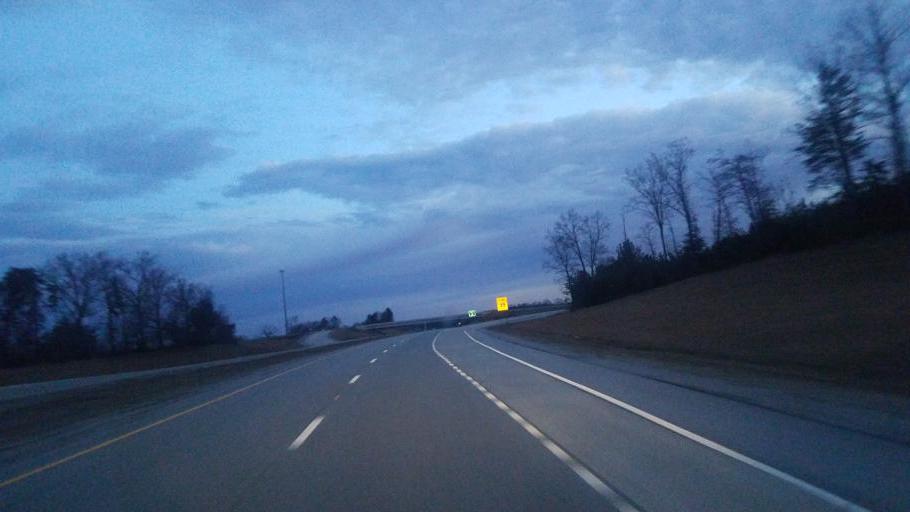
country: US
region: Tennessee
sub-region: Van Buren County
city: Spencer
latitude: 35.6250
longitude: -85.4766
